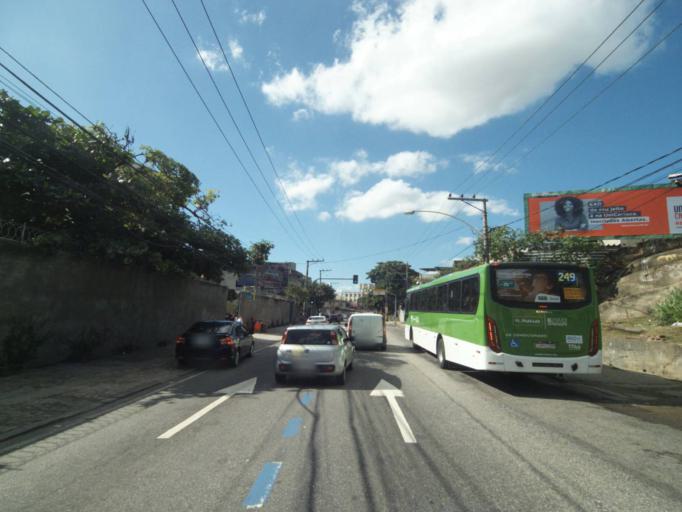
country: BR
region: Rio de Janeiro
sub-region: Rio De Janeiro
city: Rio de Janeiro
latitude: -22.9047
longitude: -43.2648
